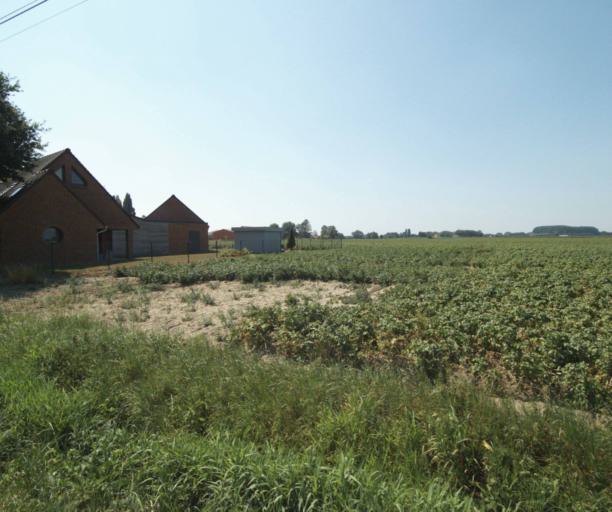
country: FR
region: Nord-Pas-de-Calais
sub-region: Departement du Nord
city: Wervicq-Sud
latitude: 50.7401
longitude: 3.0421
